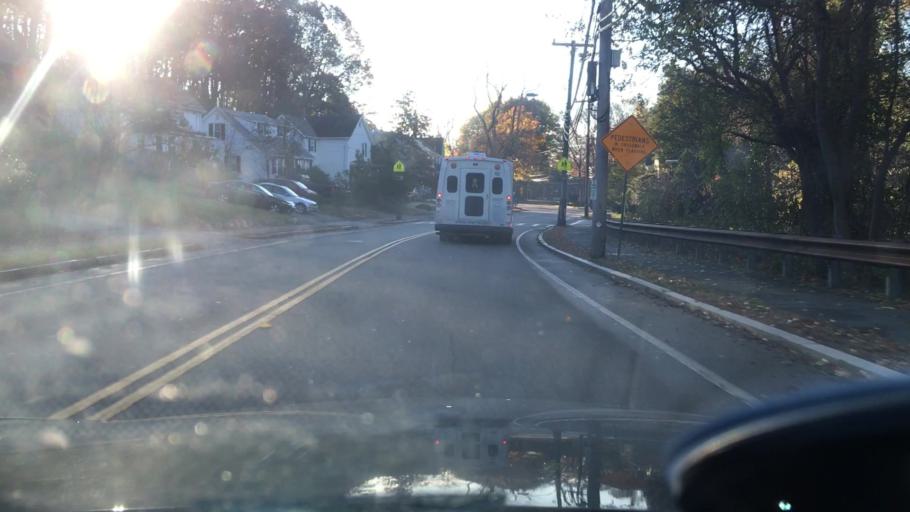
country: US
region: Massachusetts
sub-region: Norfolk County
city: Needham
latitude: 42.3220
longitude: -71.2520
